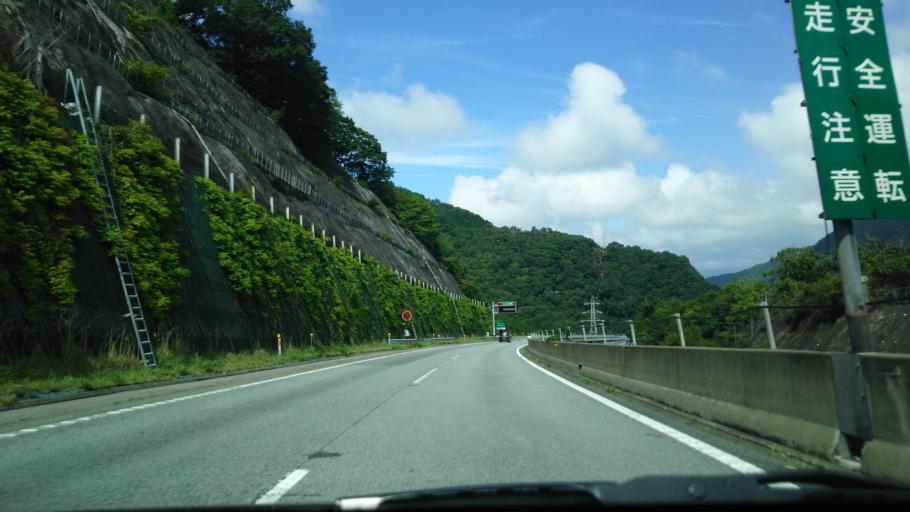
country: JP
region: Yamanashi
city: Enzan
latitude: 35.6408
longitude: 138.7703
